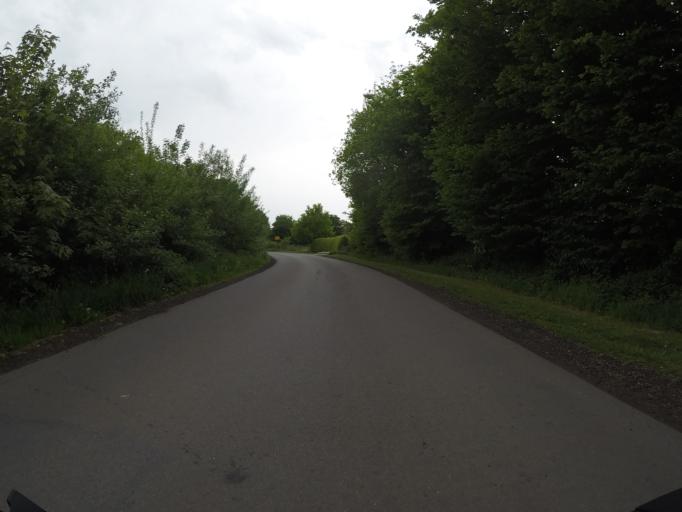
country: DE
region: Schleswig-Holstein
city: Kisdorf
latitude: 53.7851
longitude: 10.0156
